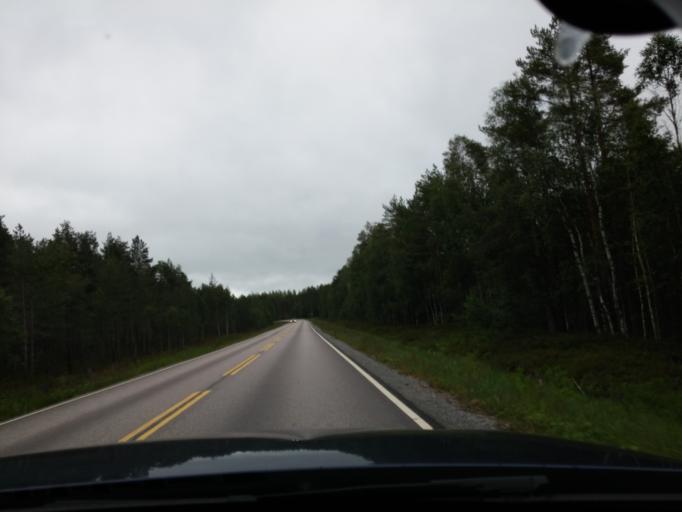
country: FI
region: Central Finland
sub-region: Saarijaervi-Viitasaari
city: Pylkoenmaeki
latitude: 62.6205
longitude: 24.7720
